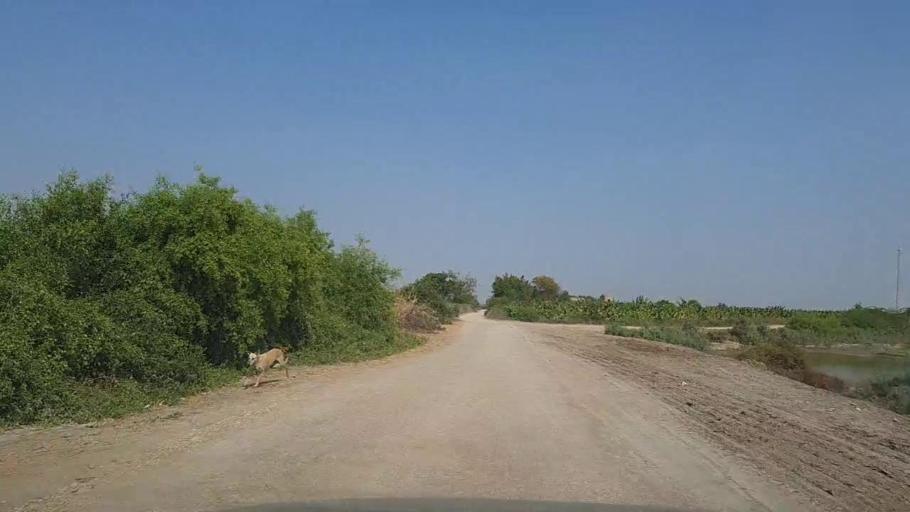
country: PK
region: Sindh
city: Thatta
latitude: 24.6120
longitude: 67.9572
